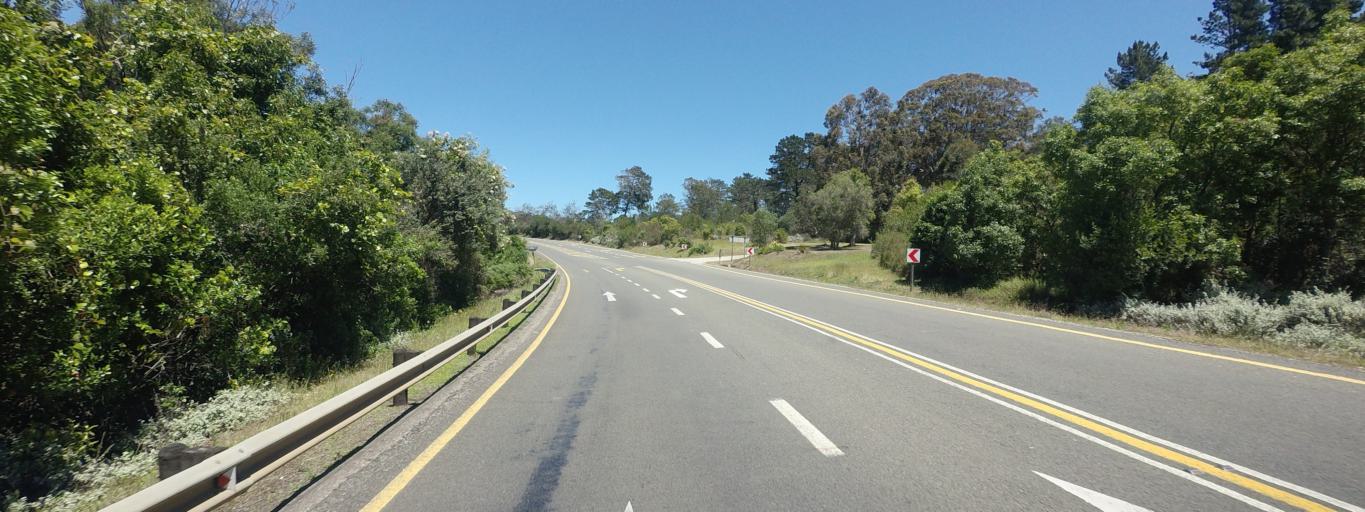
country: ZA
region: Western Cape
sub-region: Eden District Municipality
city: Plettenberg Bay
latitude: -33.9659
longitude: 23.4498
